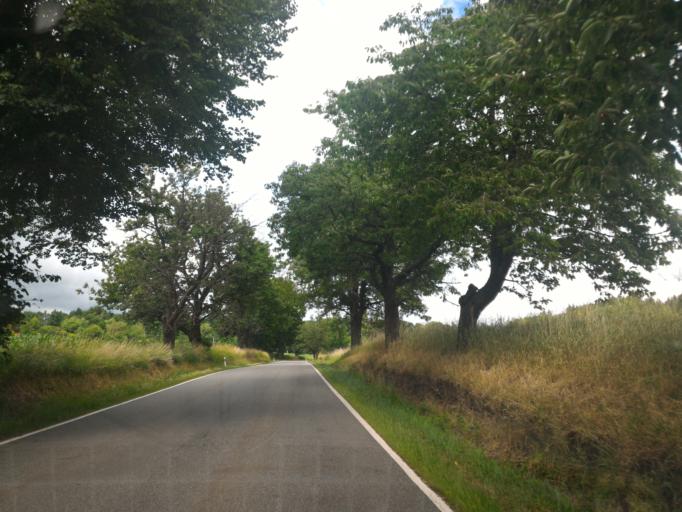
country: CZ
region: Vysocina
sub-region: Okres Jihlava
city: Telc
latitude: 49.2172
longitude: 15.4249
